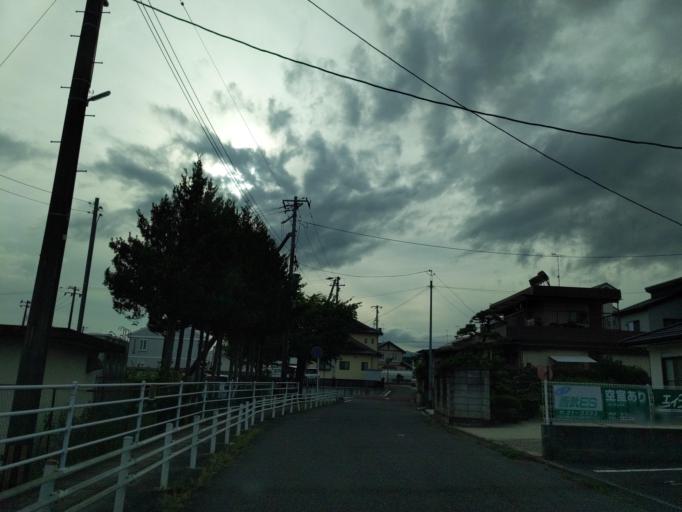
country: JP
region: Fukushima
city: Koriyama
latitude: 37.4048
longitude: 140.3315
